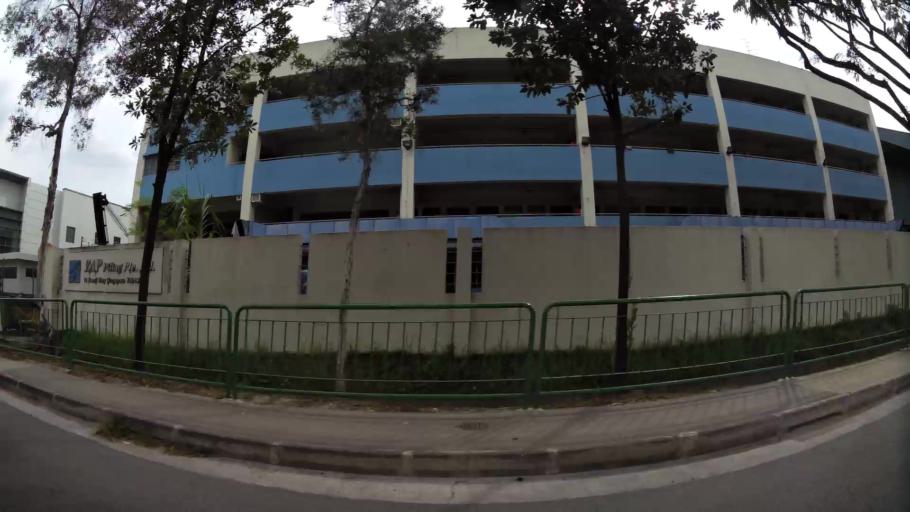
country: MY
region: Johor
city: Johor Bahru
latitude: 1.4362
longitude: 103.7474
